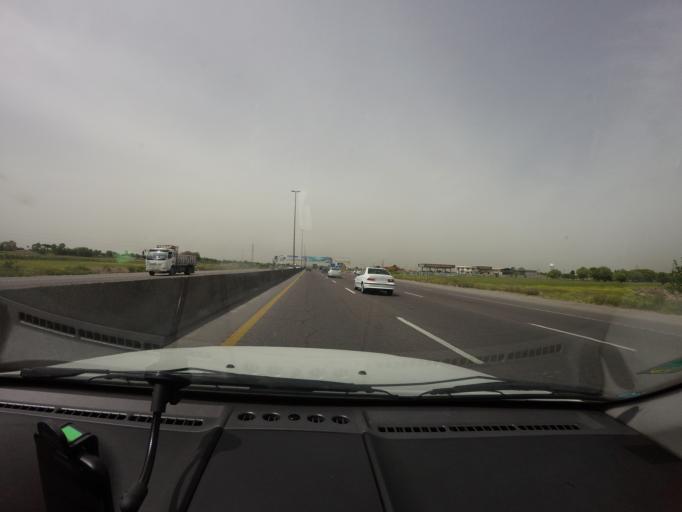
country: IR
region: Tehran
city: Eslamshahr
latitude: 35.6117
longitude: 51.2071
